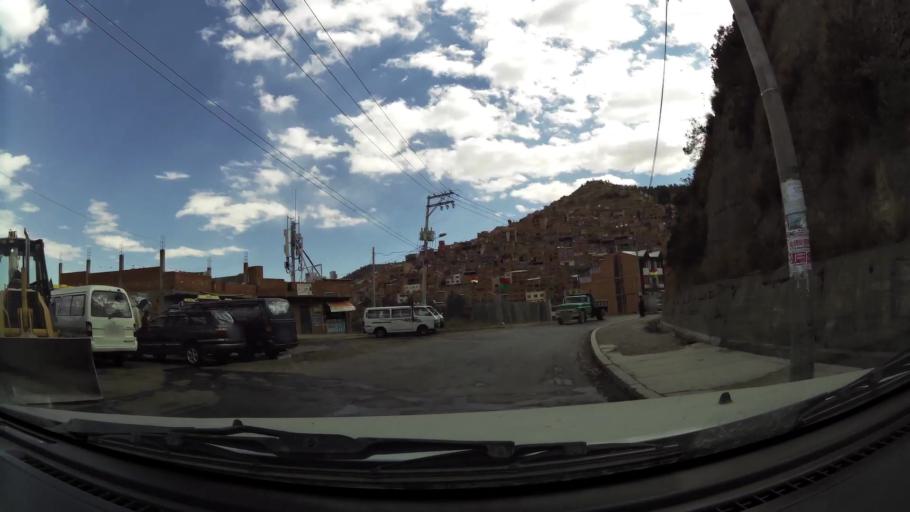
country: BO
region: La Paz
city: La Paz
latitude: -16.4693
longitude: -68.1207
